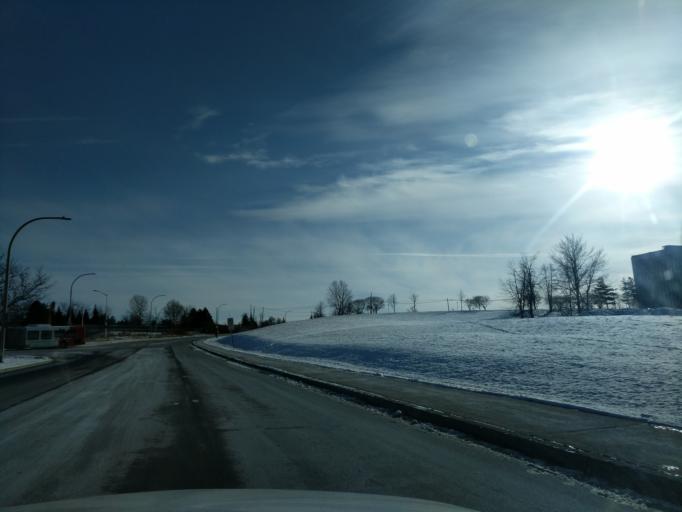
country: CA
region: Ontario
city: Ottawa
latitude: 45.3838
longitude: -75.6799
